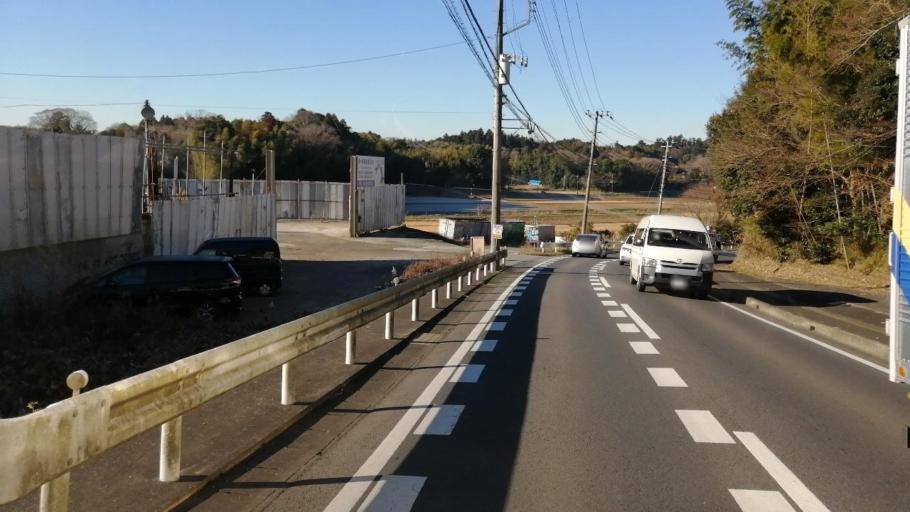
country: JP
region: Chiba
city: Narita
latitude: 35.7628
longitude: 140.3441
